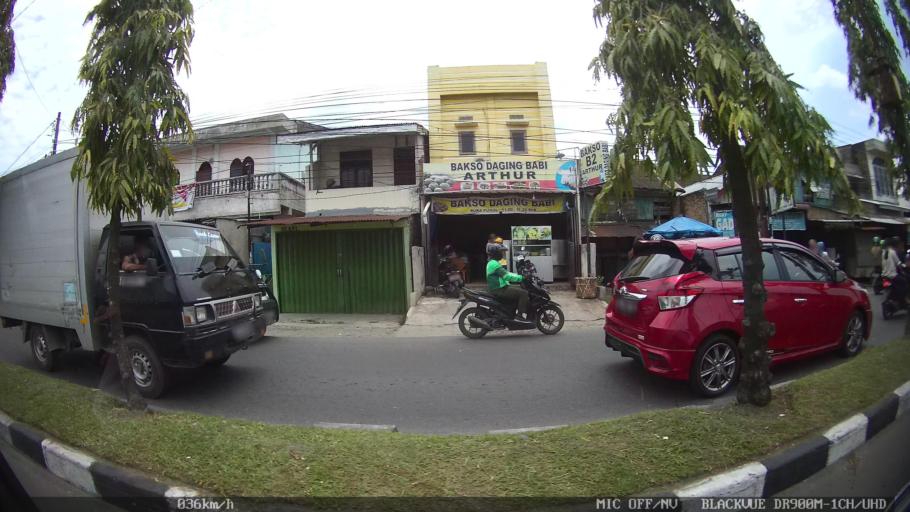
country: ID
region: North Sumatra
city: Medan
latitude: 3.5481
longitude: 98.6604
